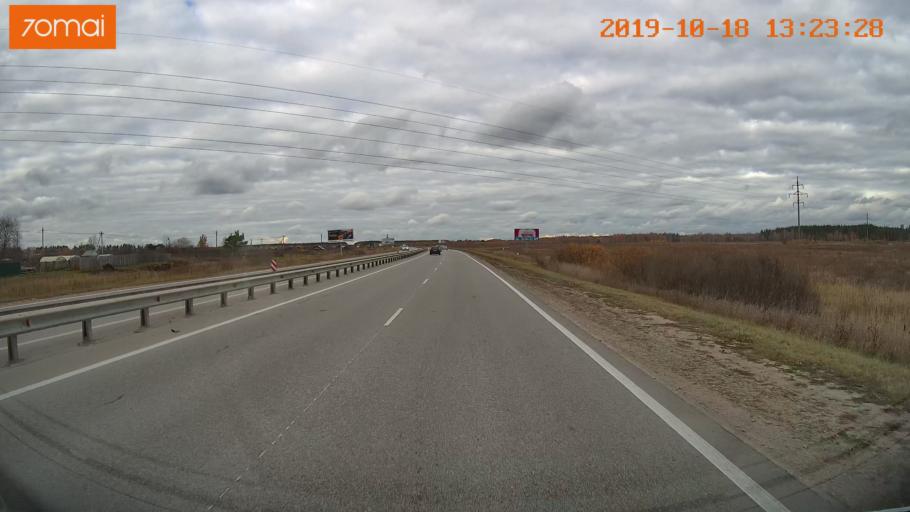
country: RU
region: Rjazan
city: Polyany
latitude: 54.7165
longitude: 39.8486
